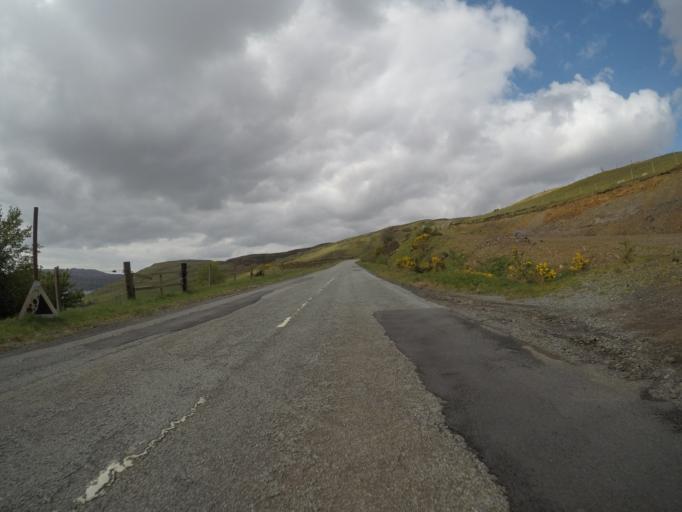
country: GB
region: Scotland
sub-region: Highland
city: Isle of Skye
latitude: 57.3020
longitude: -6.2977
